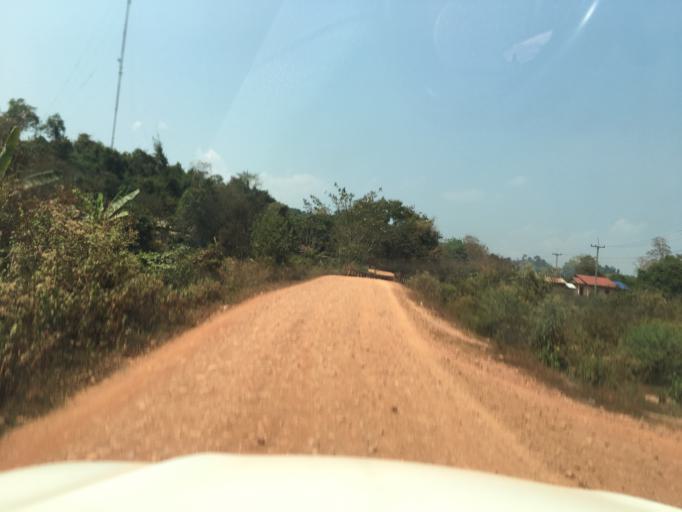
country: LA
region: Bolikhamxai
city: Bolikhan
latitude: 18.7489
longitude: 103.5970
